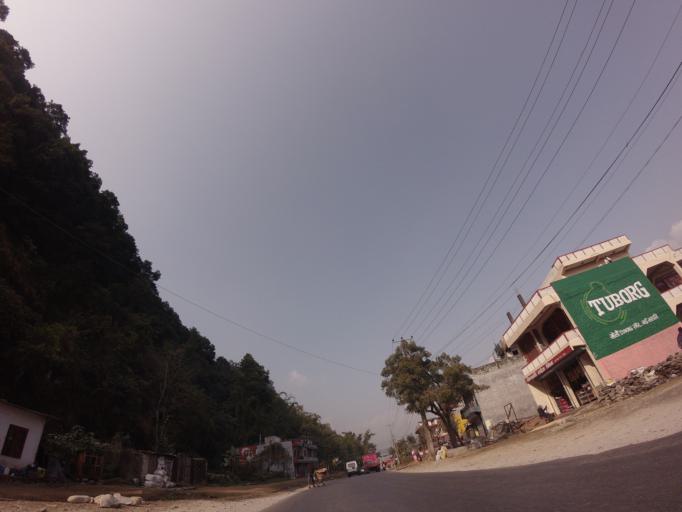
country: NP
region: Western Region
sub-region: Gandaki Zone
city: Pokhara
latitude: 28.2471
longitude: 83.9775
